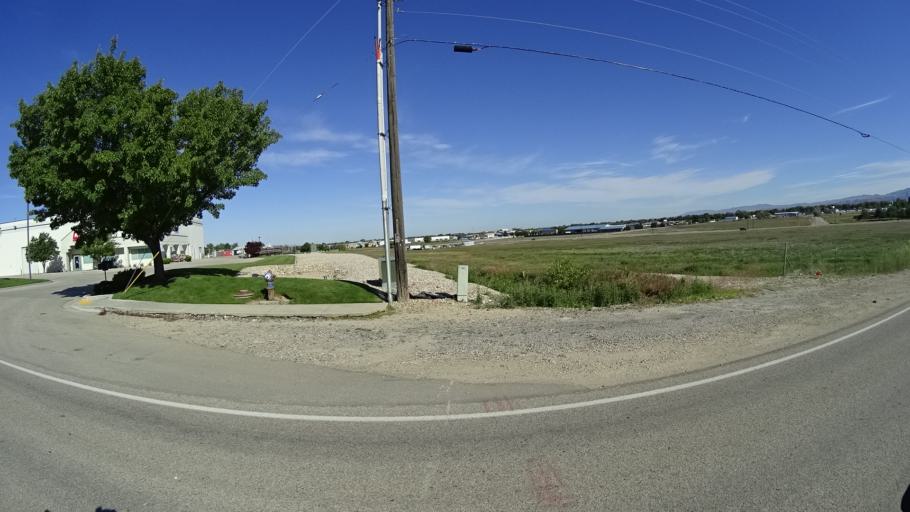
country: US
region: Idaho
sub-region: Ada County
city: Garden City
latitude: 43.5724
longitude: -116.2561
